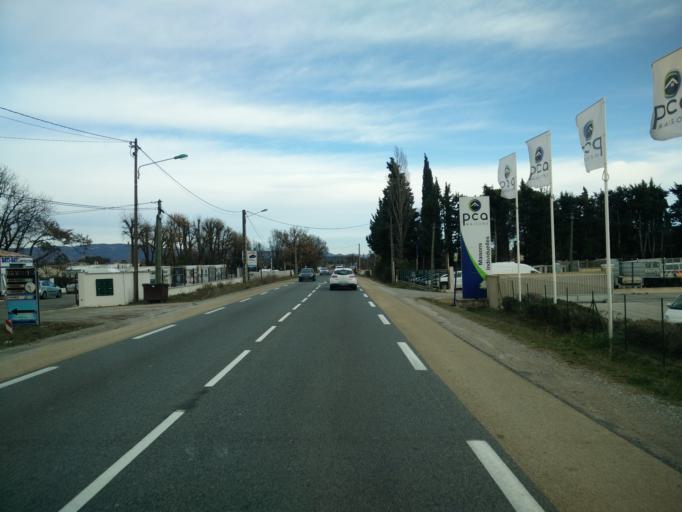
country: FR
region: Provence-Alpes-Cote d'Azur
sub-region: Departement du Var
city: La Motte
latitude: 43.4642
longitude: 6.5352
